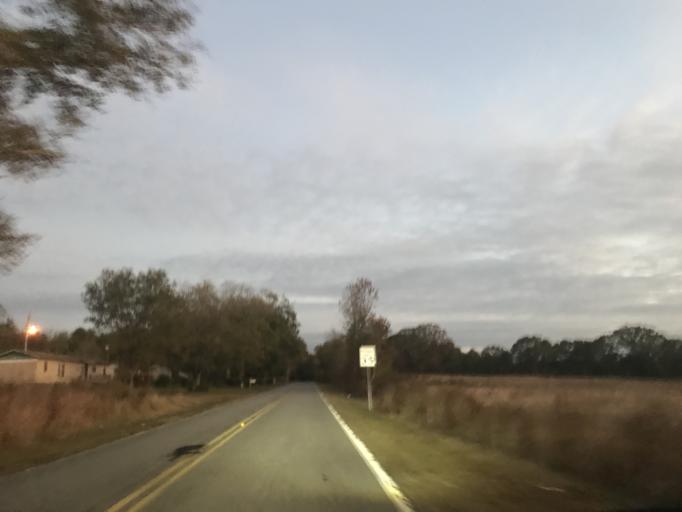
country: US
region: South Carolina
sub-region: Spartanburg County
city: Mayo
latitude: 35.0625
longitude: -81.8963
